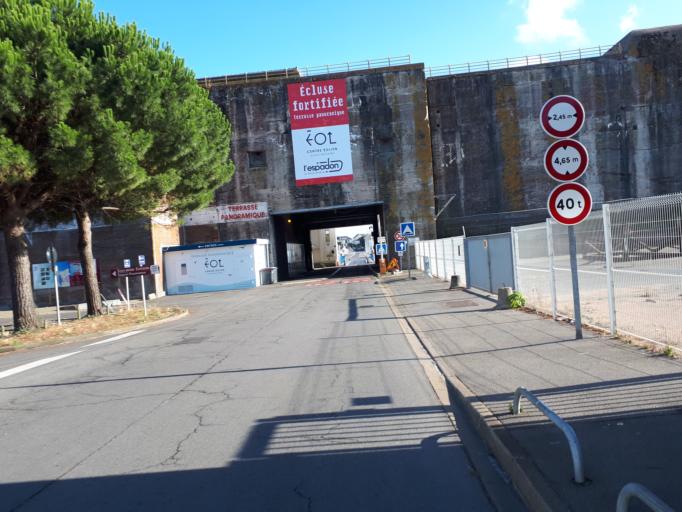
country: FR
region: Pays de la Loire
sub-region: Departement de la Loire-Atlantique
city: Saint-Nazaire
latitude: 47.2759
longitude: -2.1993
